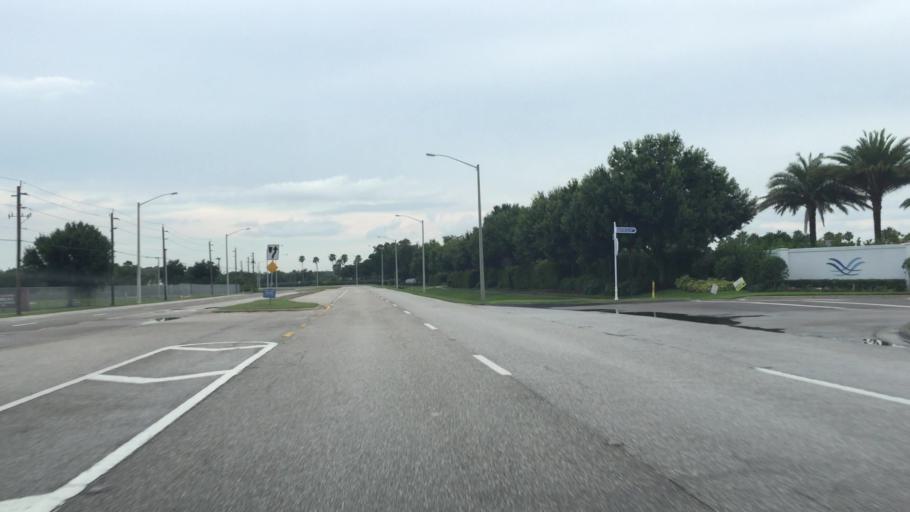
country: US
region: Florida
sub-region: Lee County
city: Fort Myers
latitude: 26.6003
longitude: -81.8180
